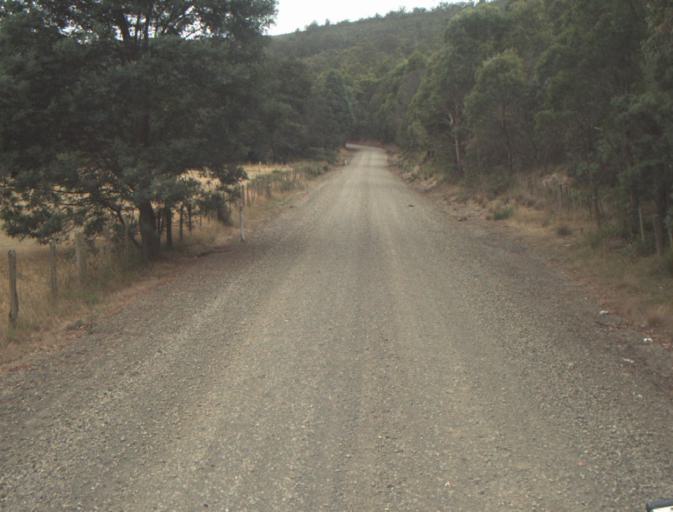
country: AU
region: Tasmania
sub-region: Northern Midlands
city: Evandale
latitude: -41.4634
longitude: 147.4956
